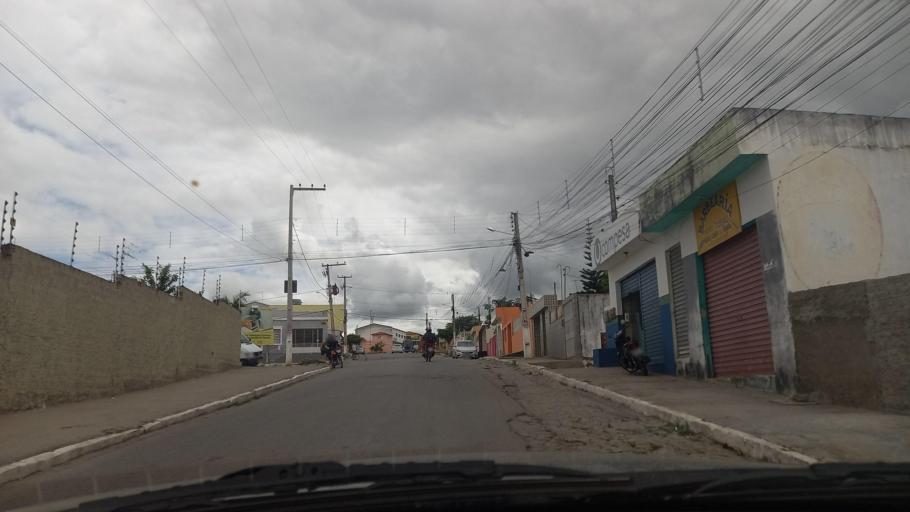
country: BR
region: Pernambuco
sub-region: Caruaru
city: Caruaru
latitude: -8.3254
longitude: -36.1382
